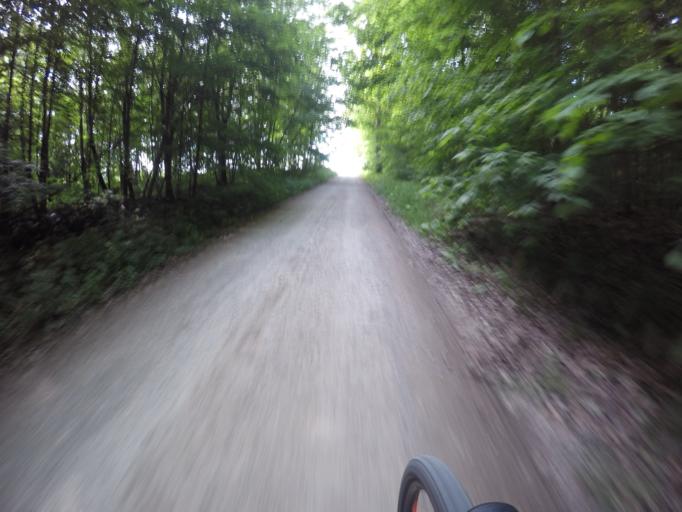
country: DE
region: Baden-Wuerttemberg
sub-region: Regierungsbezirk Stuttgart
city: Denkendorf
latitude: 48.6670
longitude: 9.3201
